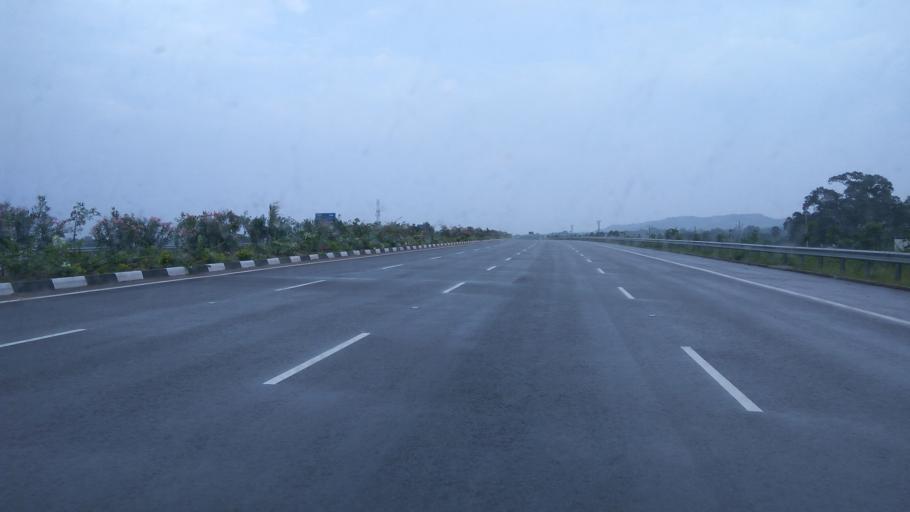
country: IN
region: Telangana
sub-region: Rangareddi
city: Ghatkesar
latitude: 17.4639
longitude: 78.6705
